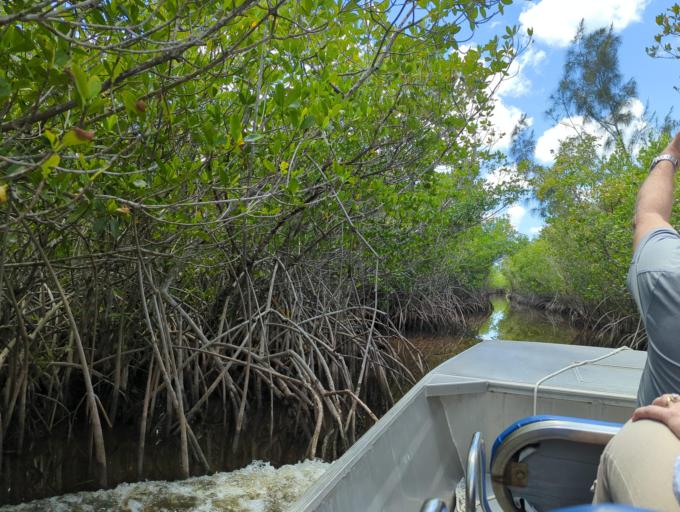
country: US
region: Florida
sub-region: Collier County
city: Marco
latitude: 25.9061
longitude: -81.3745
